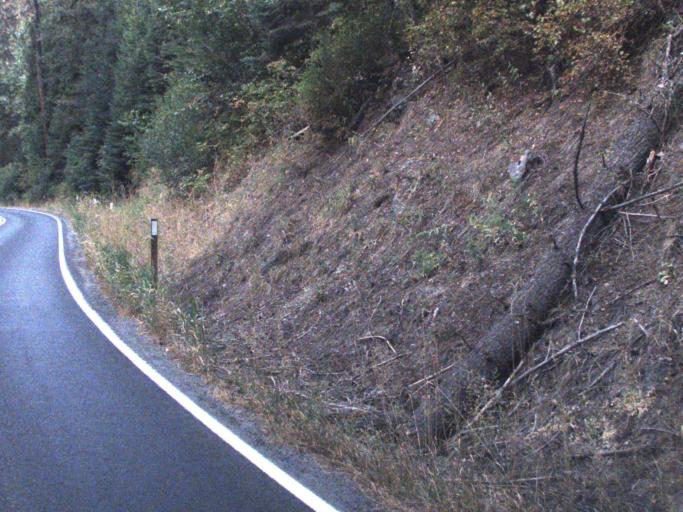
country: US
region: Washington
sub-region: Spokane County
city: Trentwood
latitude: 47.8362
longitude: -117.1834
